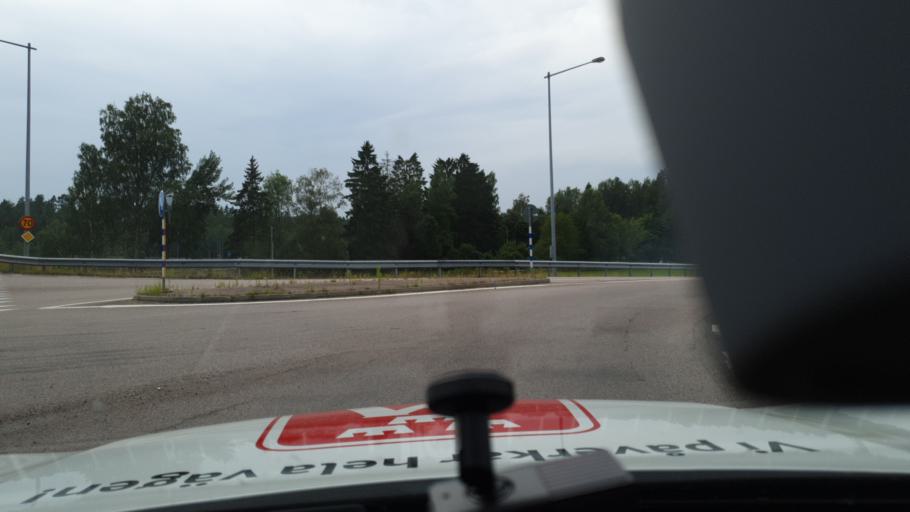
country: SE
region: Vaermland
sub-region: Karlstads Kommun
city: Karlstad
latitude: 59.4294
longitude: 13.4574
